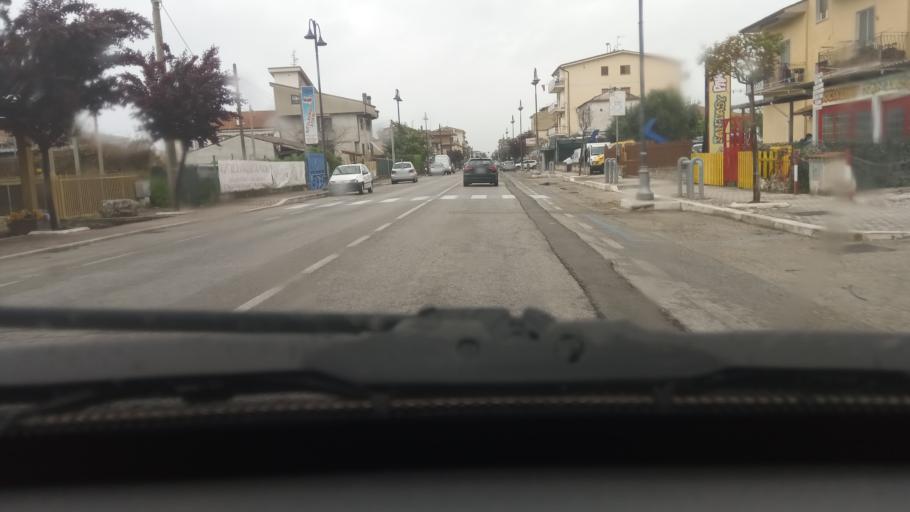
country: IT
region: Latium
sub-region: Provincia di Latina
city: Minturno
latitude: 41.2478
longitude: 13.7454
